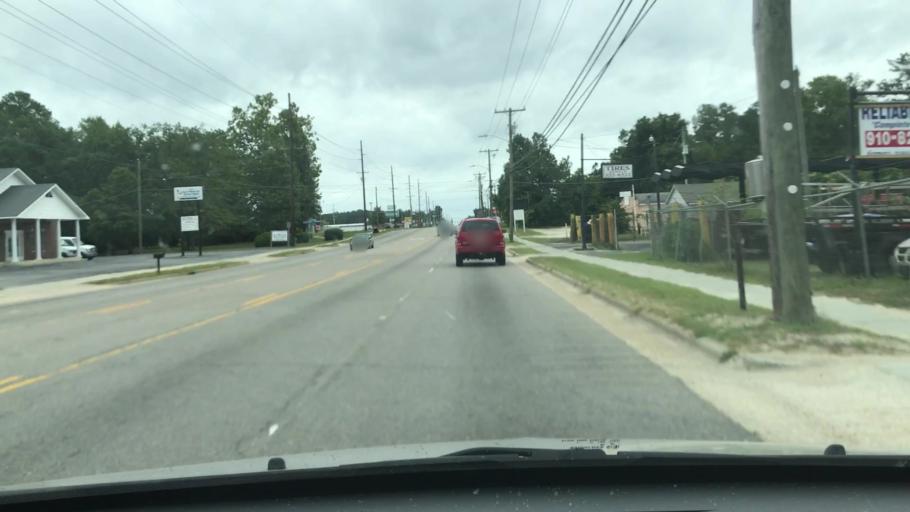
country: US
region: North Carolina
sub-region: Cumberland County
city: Fayetteville
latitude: 35.1016
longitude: -78.9196
